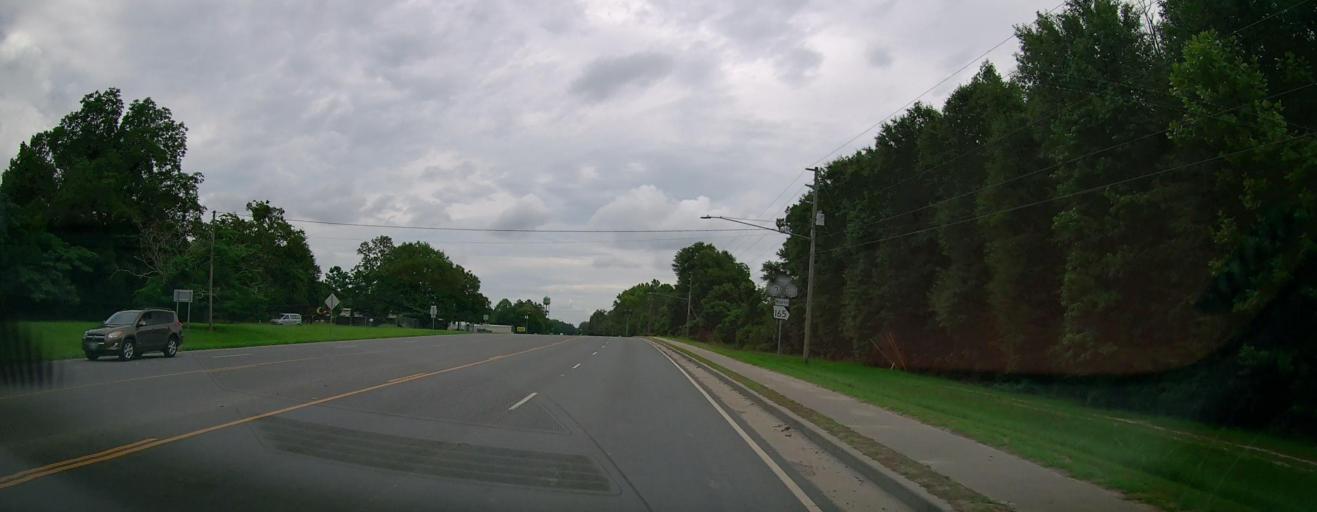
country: US
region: Georgia
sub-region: Dodge County
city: Eastman
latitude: 32.1062
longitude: -83.0736
